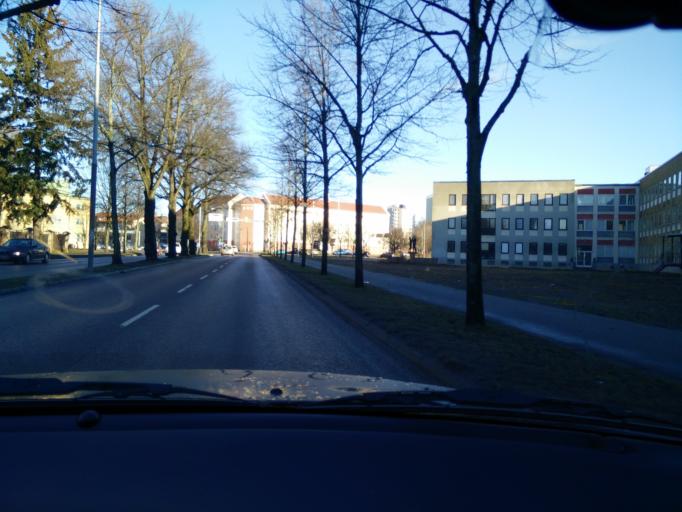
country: SE
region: Vaestmanland
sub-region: Vasteras
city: Vasteras
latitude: 59.6153
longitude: 16.5542
